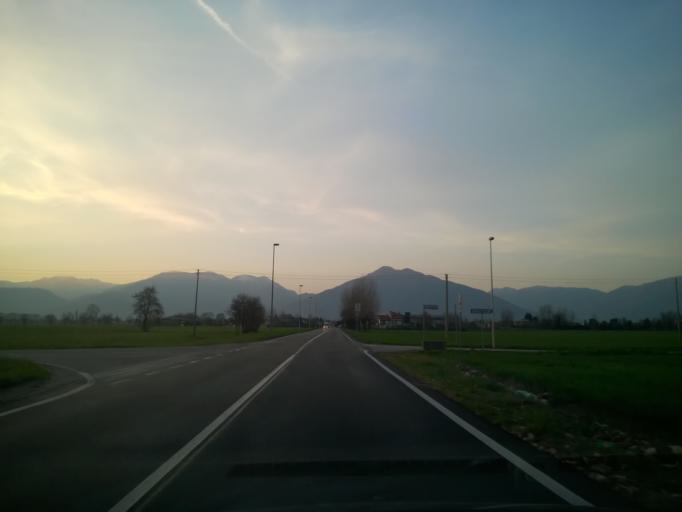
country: IT
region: Veneto
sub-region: Provincia di Vicenza
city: Marano Vicentino
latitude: 45.6832
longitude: 11.4510
